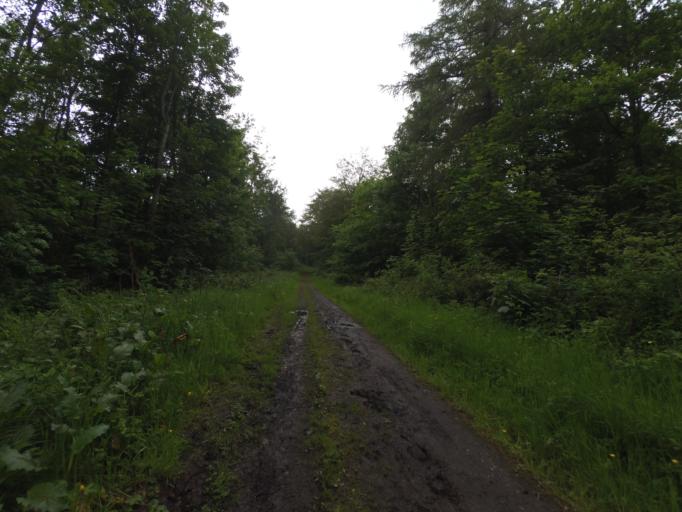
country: GB
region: Scotland
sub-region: East Lothian
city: Musselburgh
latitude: 55.9118
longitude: -3.0105
